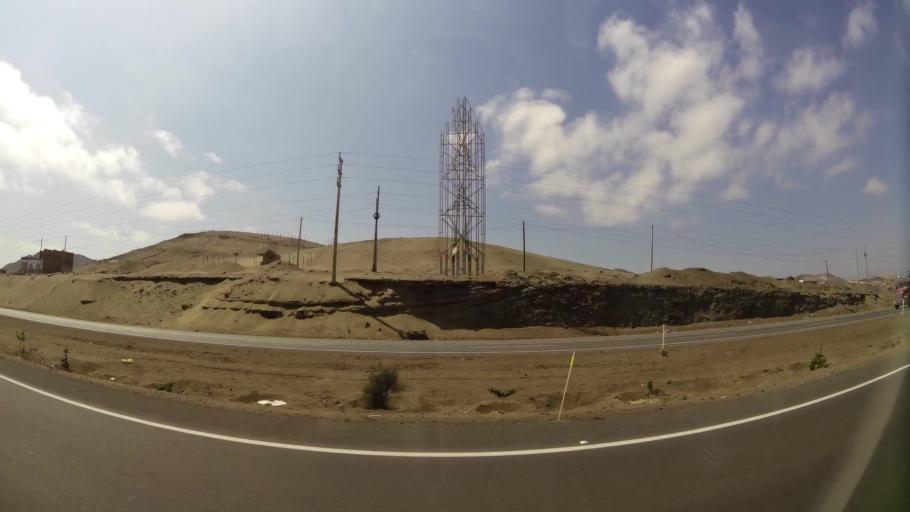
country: PE
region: Lima
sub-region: Provincia de Canete
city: Asia
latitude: -12.7545
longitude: -76.6056
